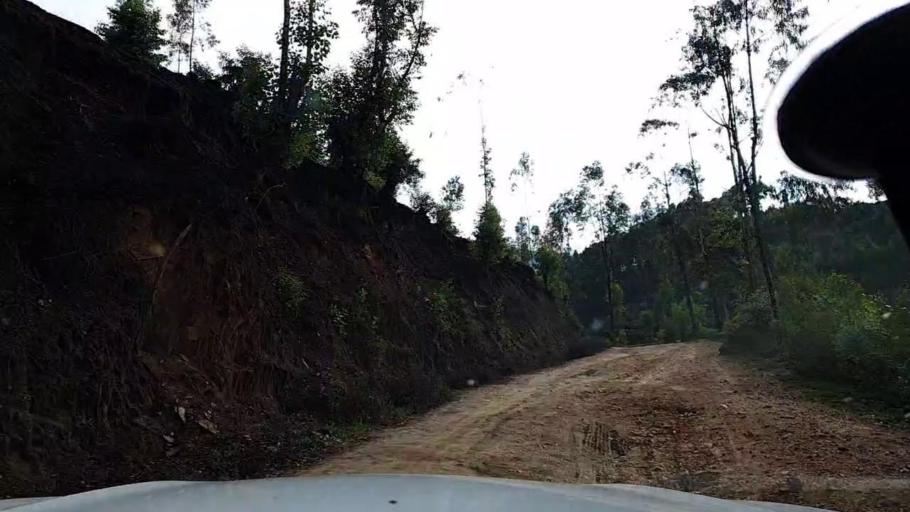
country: RW
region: Southern Province
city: Gitarama
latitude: -2.1688
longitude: 29.5548
